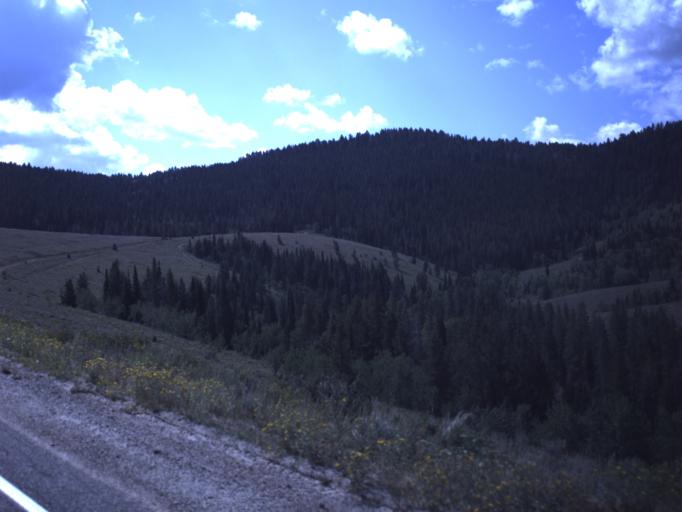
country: US
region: Idaho
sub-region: Bear Lake County
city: Paris
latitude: 41.9552
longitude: -111.4984
